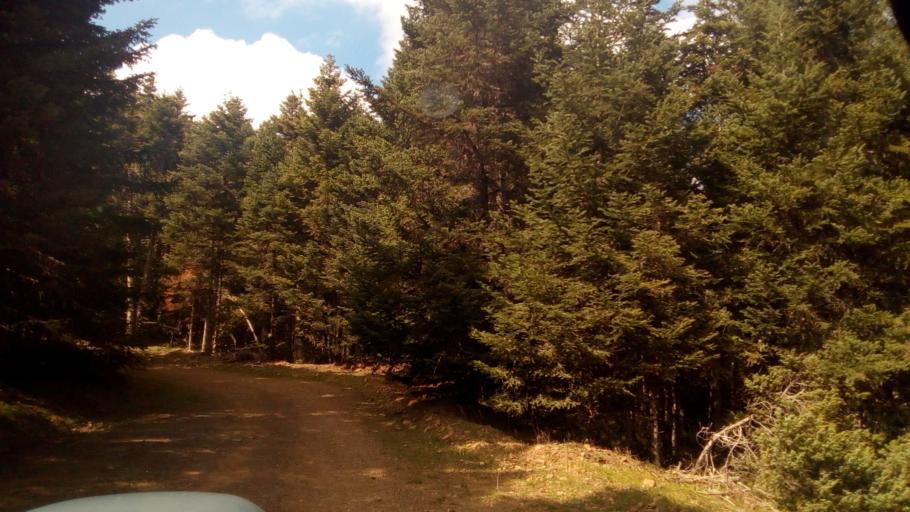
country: GR
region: West Greece
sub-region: Nomos Aitolias kai Akarnanias
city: Nafpaktos
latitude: 38.6386
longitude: 21.9477
